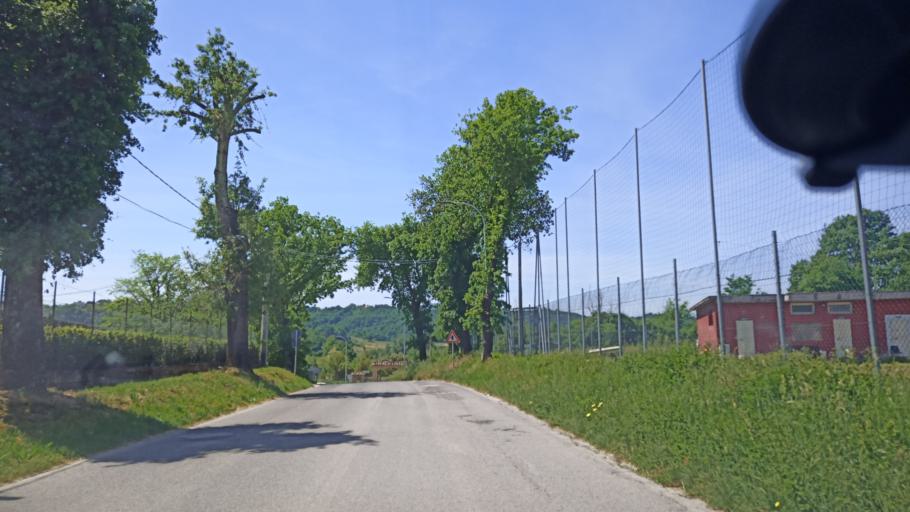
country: IT
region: Latium
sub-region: Provincia di Rieti
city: Forano
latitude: 42.3210
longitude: 12.5872
